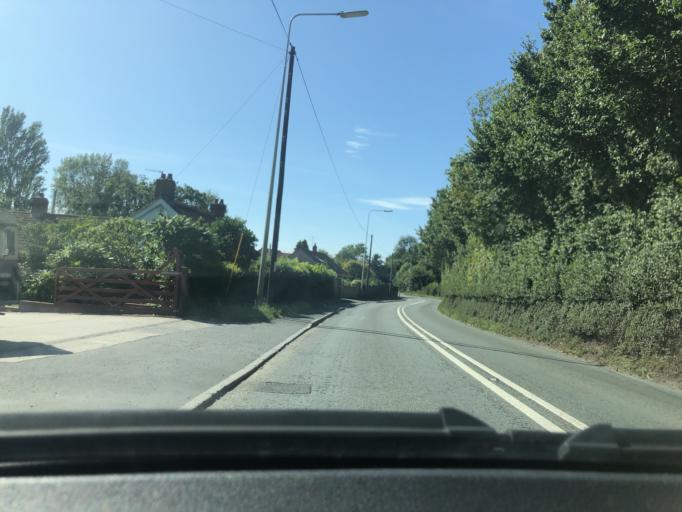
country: GB
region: England
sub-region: Somerset
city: Woolavington
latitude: 51.1547
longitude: -2.9546
